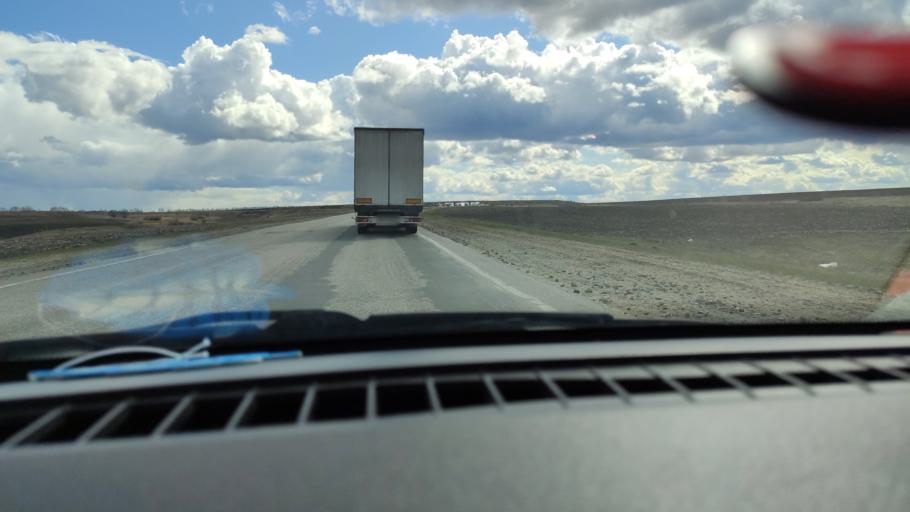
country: RU
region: Samara
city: Syzran'
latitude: 53.0068
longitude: 48.3320
